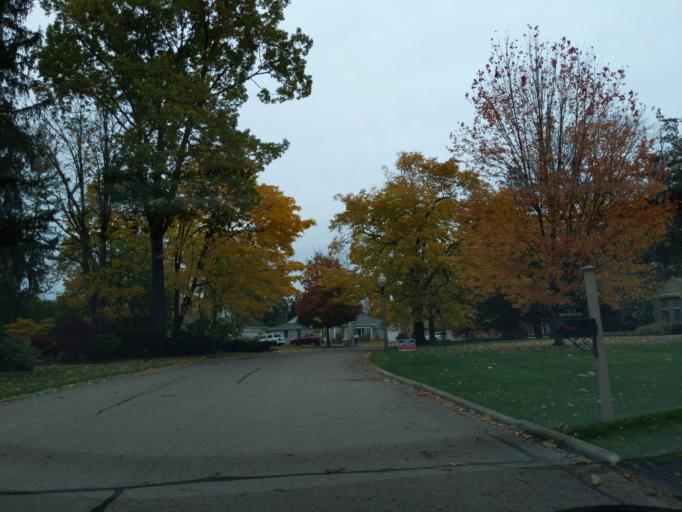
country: US
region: Michigan
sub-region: Ingham County
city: Edgemont Park
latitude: 42.7134
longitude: -84.5925
